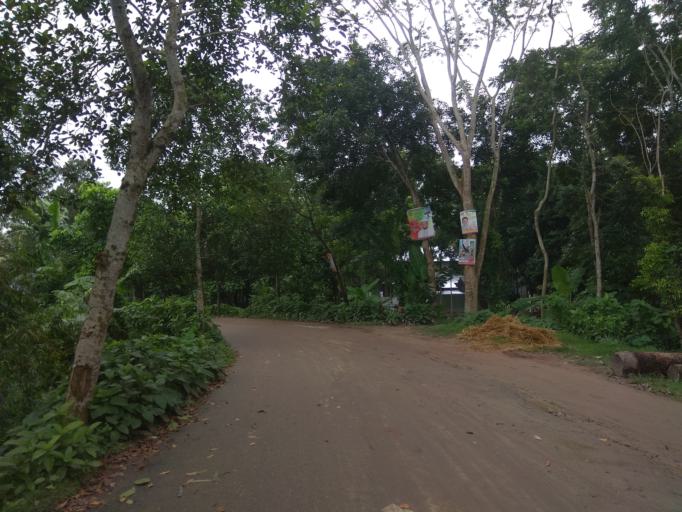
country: BD
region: Dhaka
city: Dohar
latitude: 23.4175
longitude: 90.0708
